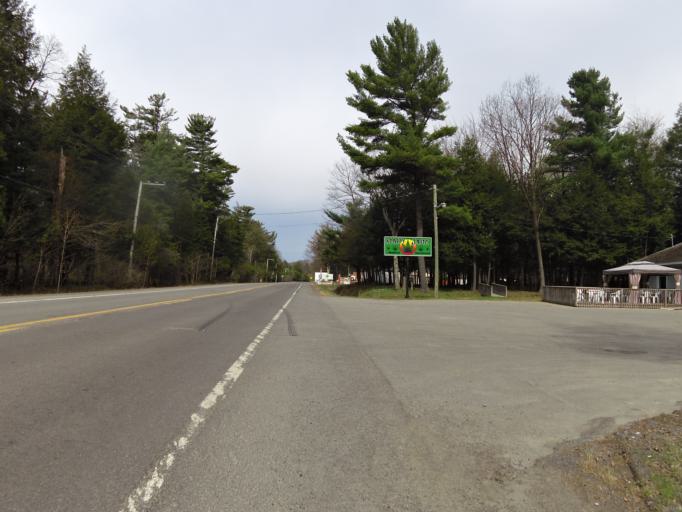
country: CA
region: Quebec
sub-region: Laurentides
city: Oka
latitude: 45.4664
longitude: -74.1092
